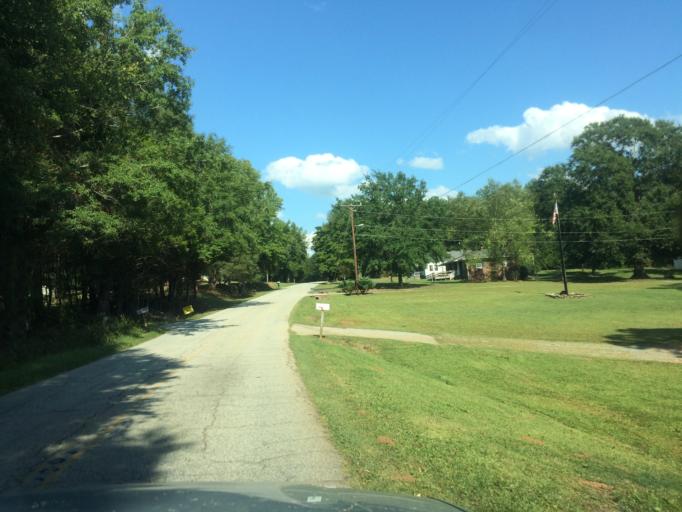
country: US
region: South Carolina
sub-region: Greenwood County
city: Ware Shoals
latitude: 34.4349
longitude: -82.2579
